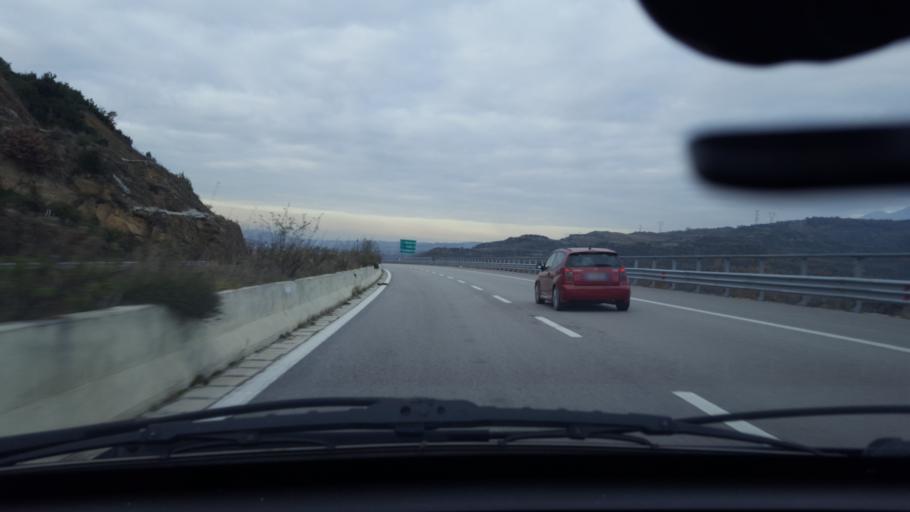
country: AL
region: Tirane
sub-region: Rrethi i Tiranes
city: Berzhite
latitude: 41.2312
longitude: 19.9288
